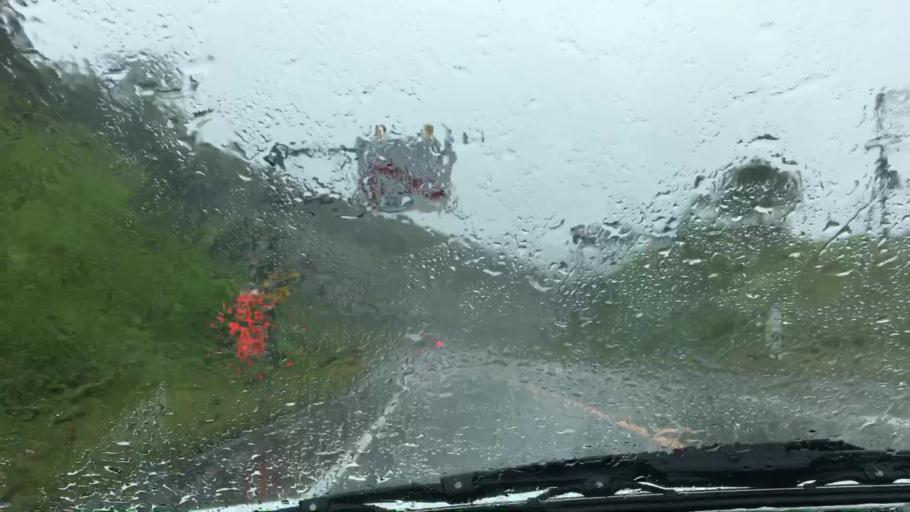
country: JP
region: Hokkaido
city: Sapporo
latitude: 42.8483
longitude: 141.0833
